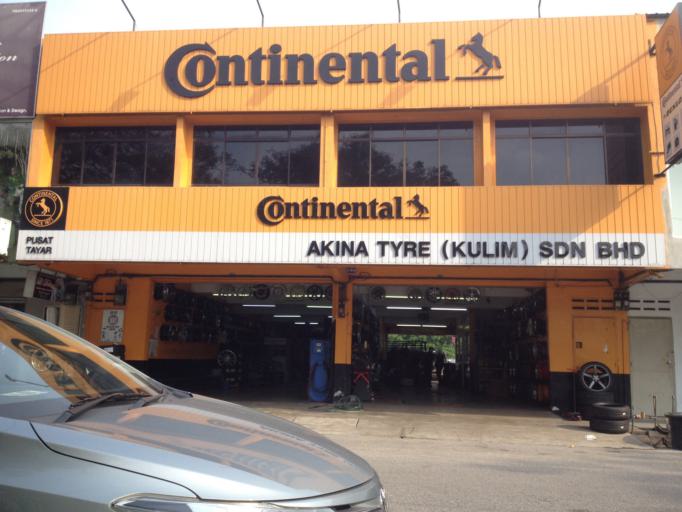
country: MY
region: Kedah
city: Kulim
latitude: 5.3780
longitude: 100.5419
